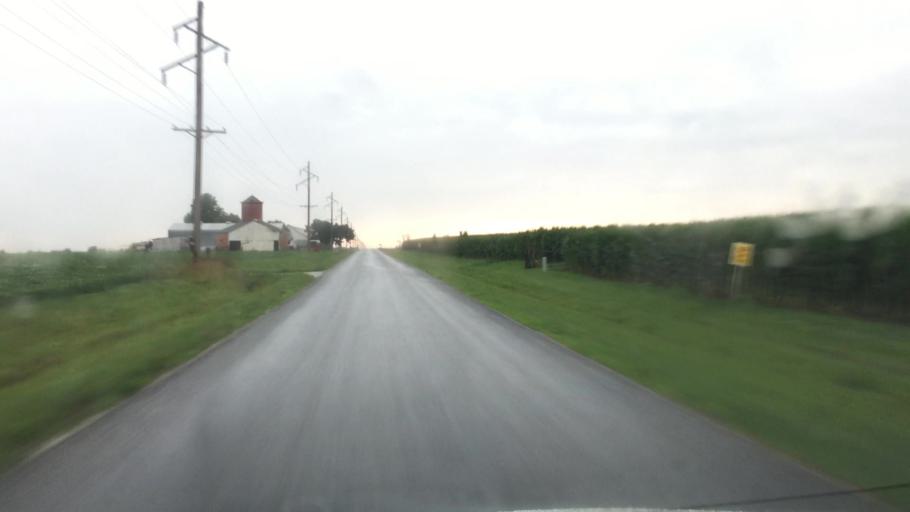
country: US
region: Illinois
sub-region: Hancock County
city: Hamilton
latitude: 40.4987
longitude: -91.2700
